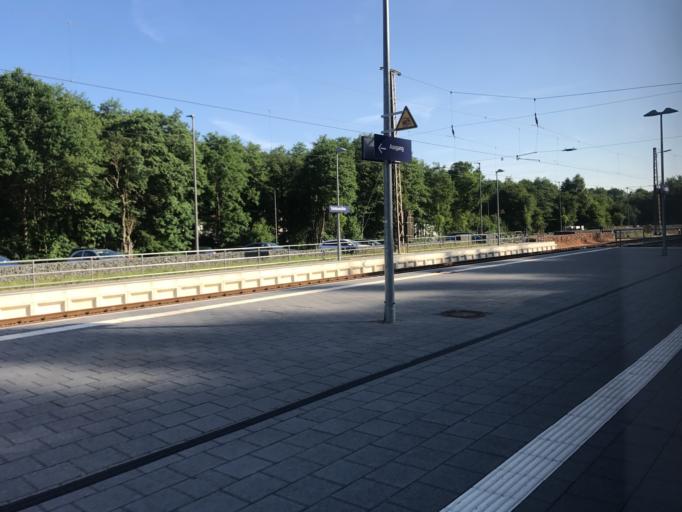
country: DE
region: Saarland
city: Nohfelden
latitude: 49.5813
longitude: 7.1158
